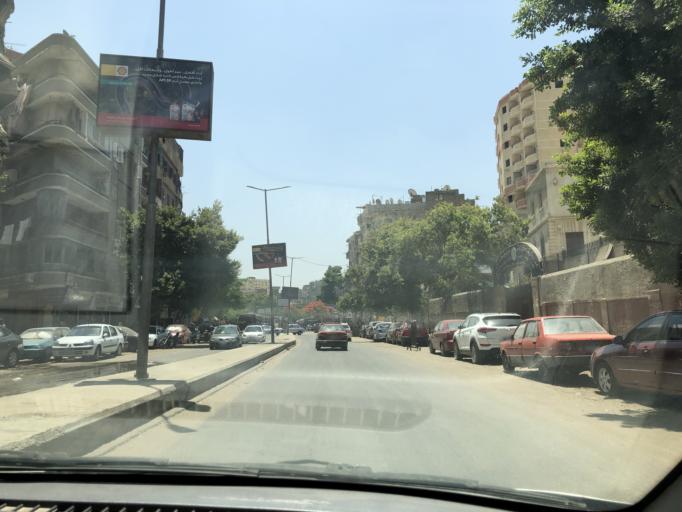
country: EG
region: Muhafazat al Qahirah
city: Cairo
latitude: 30.0686
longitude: 31.2705
